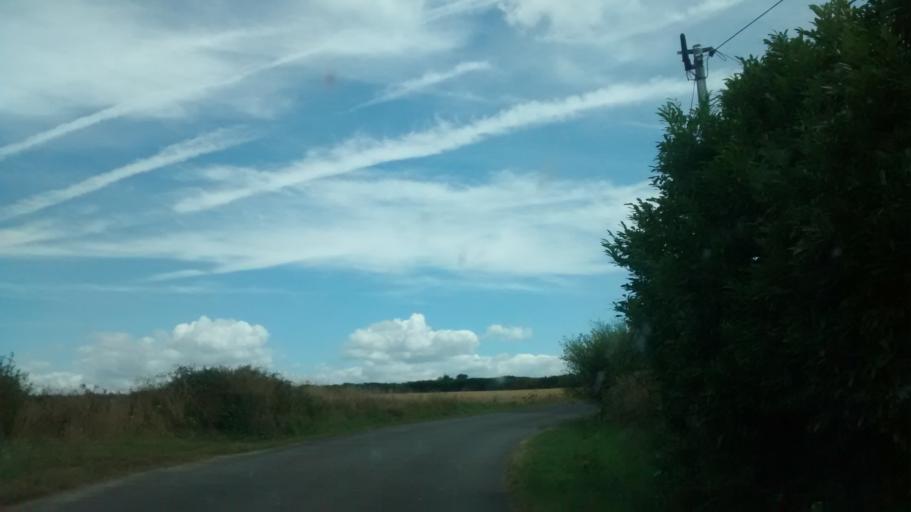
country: FR
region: Brittany
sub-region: Departement du Finistere
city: Plouguerneau
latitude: 48.6226
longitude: -4.4714
